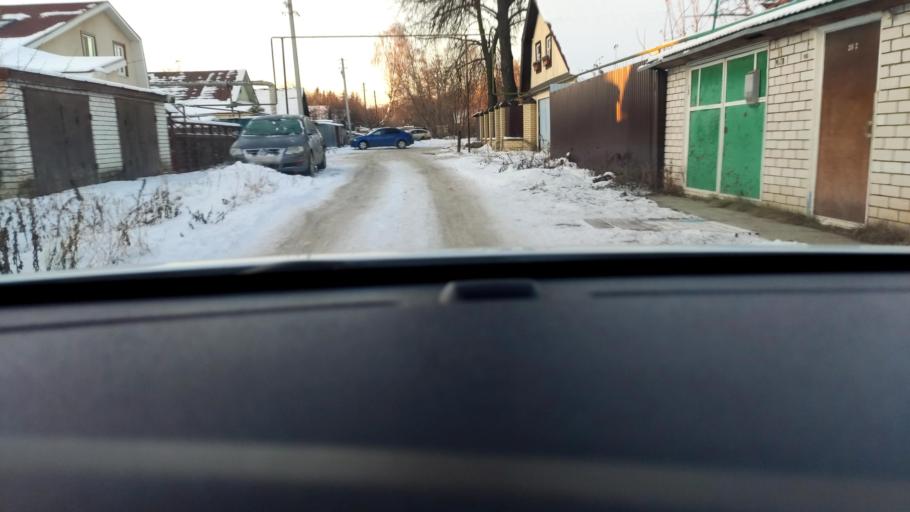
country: RU
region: Tatarstan
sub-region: Gorod Kazan'
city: Kazan
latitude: 55.8064
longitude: 49.0810
